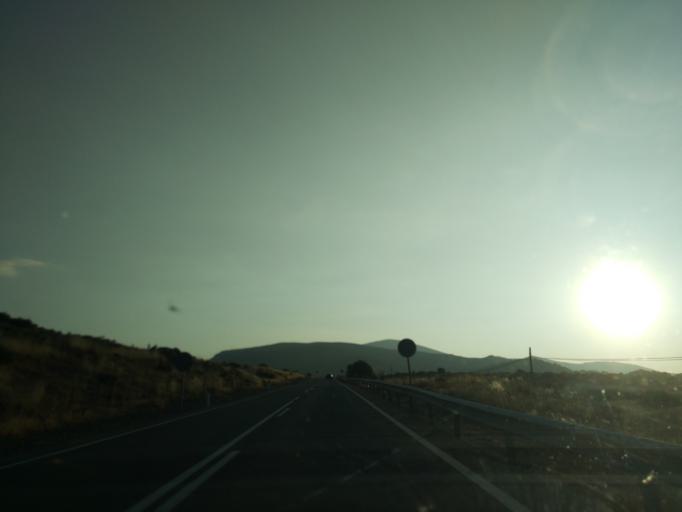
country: ES
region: Castille and Leon
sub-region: Provincia de Avila
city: Narros del Puerto
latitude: 40.5238
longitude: -4.9752
